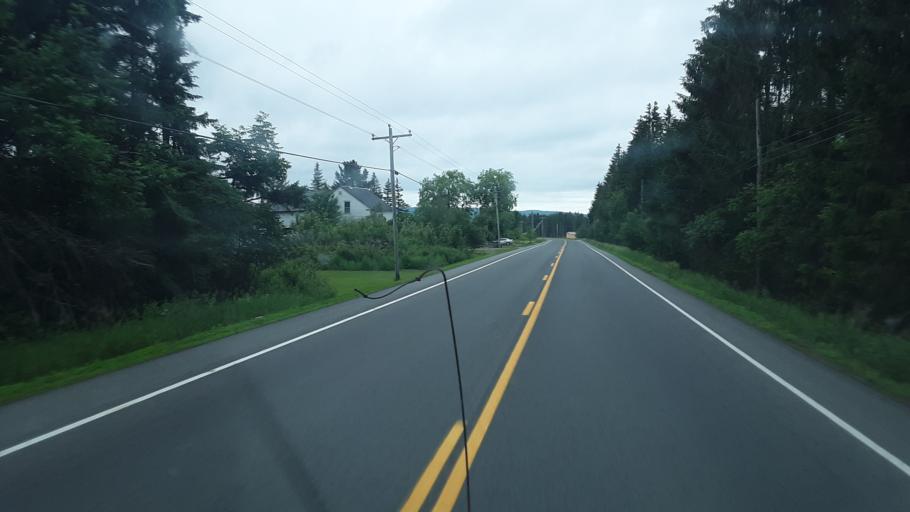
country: US
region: Maine
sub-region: Penobscot County
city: Patten
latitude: 45.9475
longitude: -68.4528
